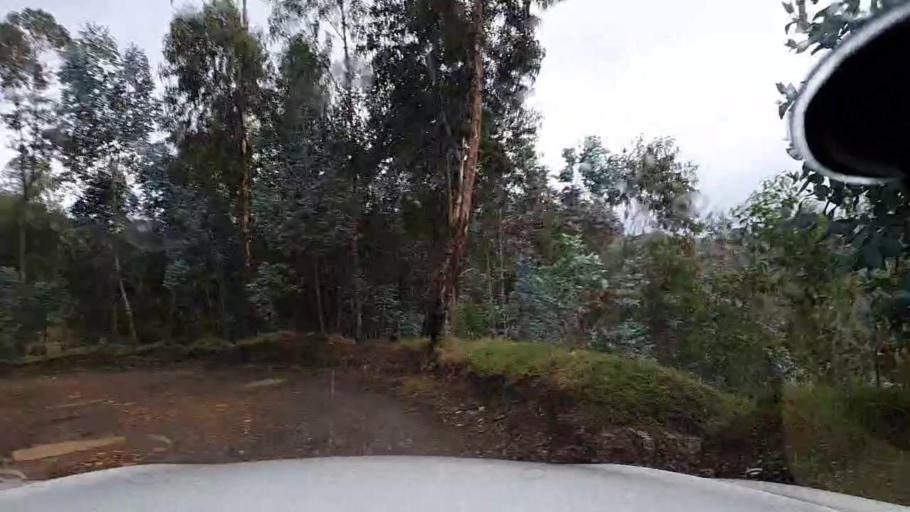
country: RW
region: Western Province
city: Kibuye
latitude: -2.0771
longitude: 29.5134
